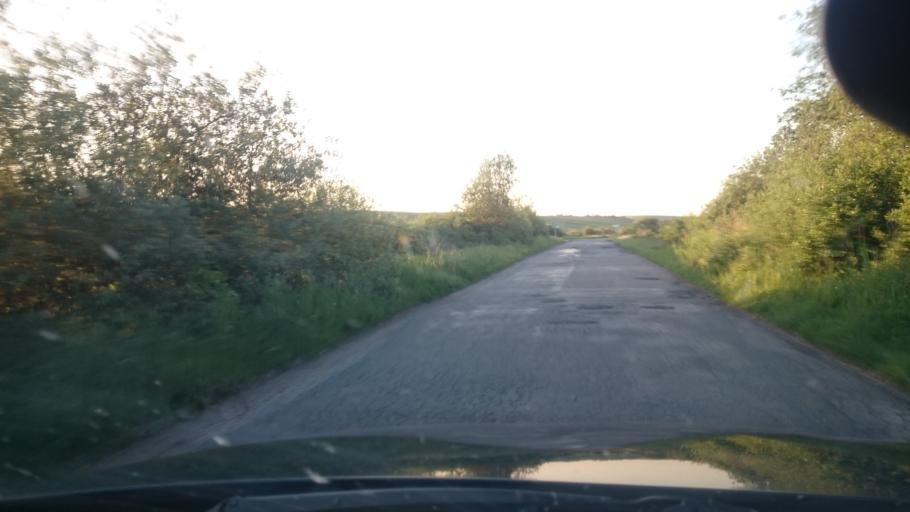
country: PL
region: Lower Silesian Voivodeship
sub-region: Powiat zabkowicki
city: Zloty Stok
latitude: 50.4822
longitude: 16.8465
